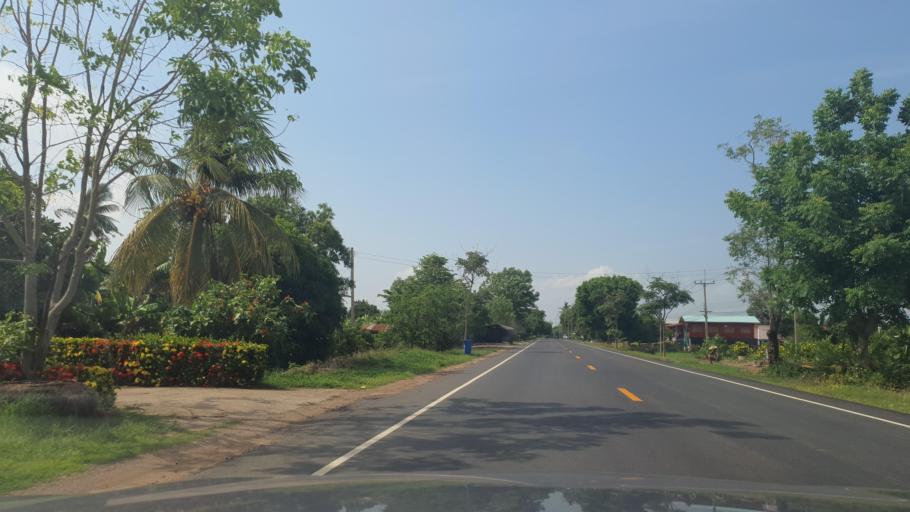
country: TH
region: Sukhothai
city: Si Samrong
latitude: 17.1546
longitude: 99.8265
